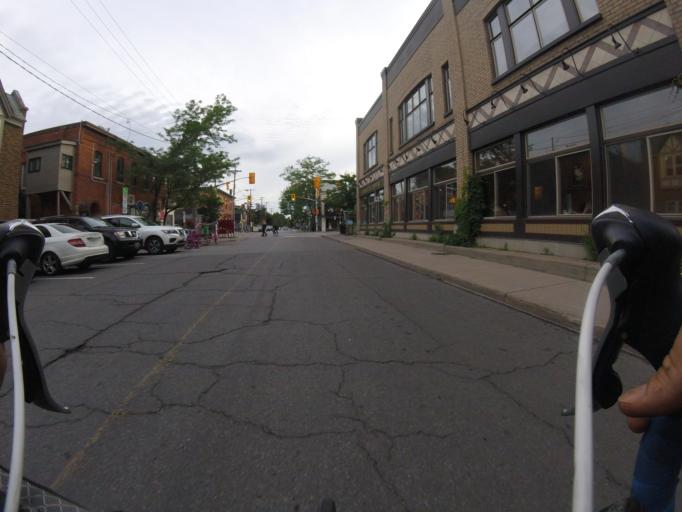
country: CA
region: Ontario
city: Ottawa
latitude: 45.4033
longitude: -75.6879
